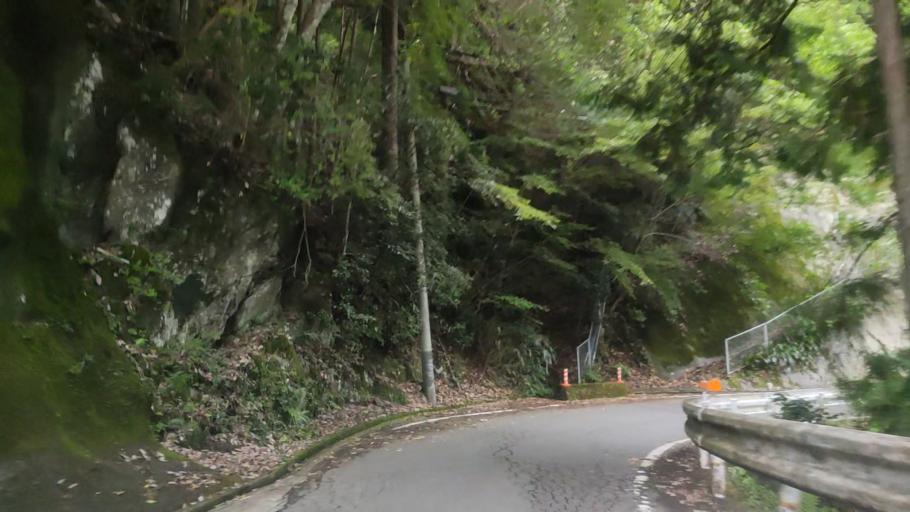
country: JP
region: Wakayama
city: Koya
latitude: 34.2299
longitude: 135.6369
